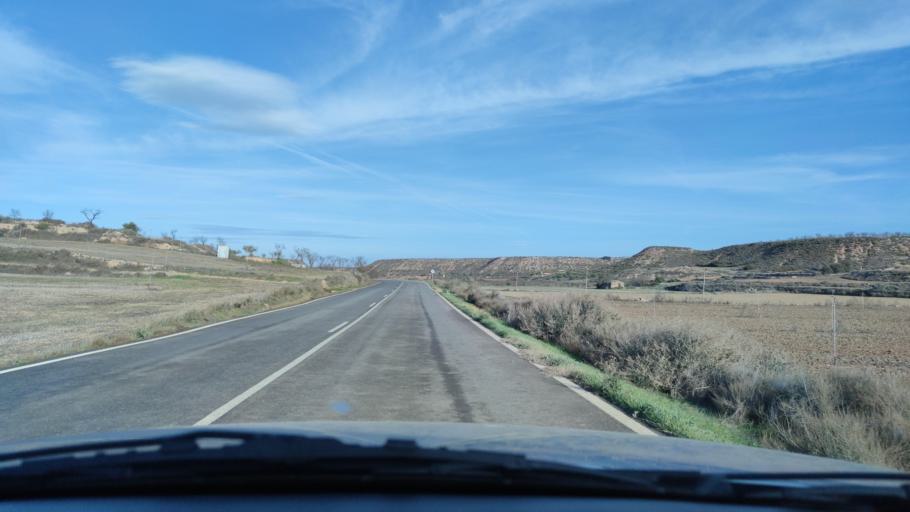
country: ES
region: Catalonia
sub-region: Provincia de Lleida
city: Alcano
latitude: 41.4868
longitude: 0.6160
